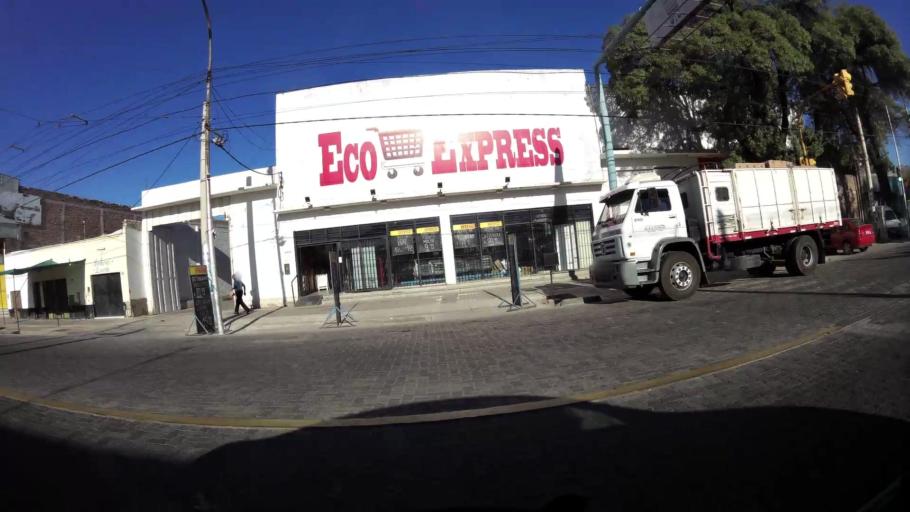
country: AR
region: Mendoza
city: Las Heras
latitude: -32.8596
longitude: -68.8331
